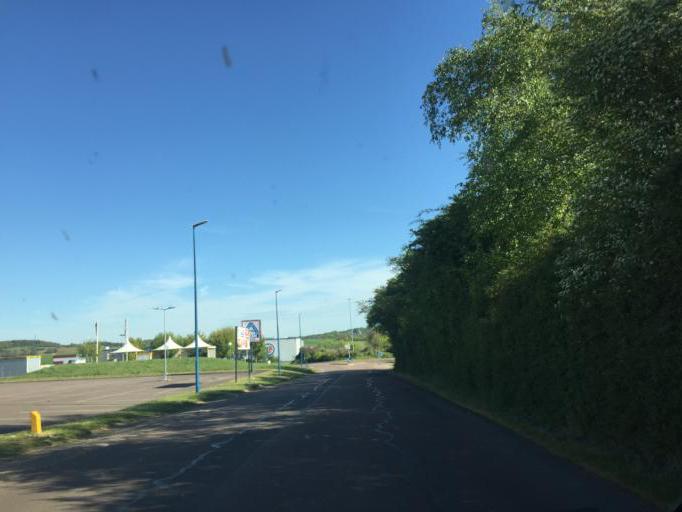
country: FR
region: Bourgogne
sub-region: Departement de la Nievre
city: Clamecy
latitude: 47.4724
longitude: 3.5208
